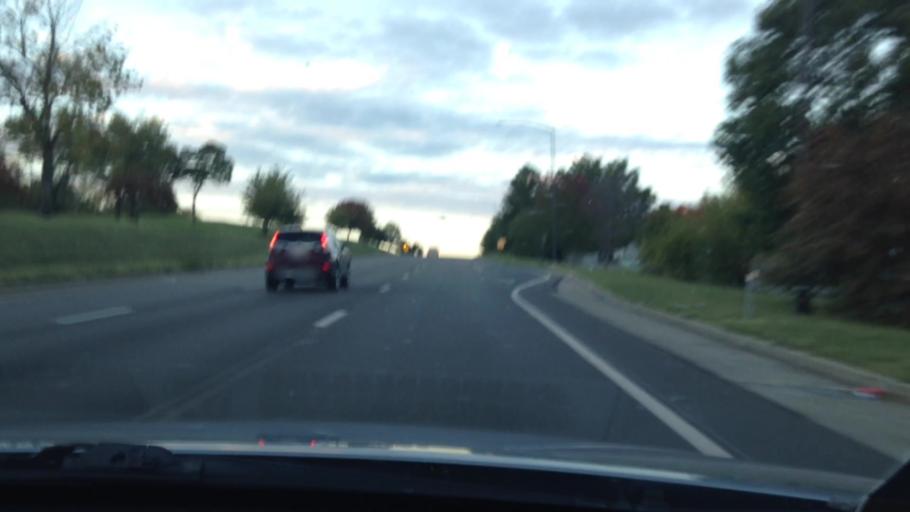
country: US
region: Kansas
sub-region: Johnson County
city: Mission Hills
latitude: 39.0221
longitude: -94.5536
